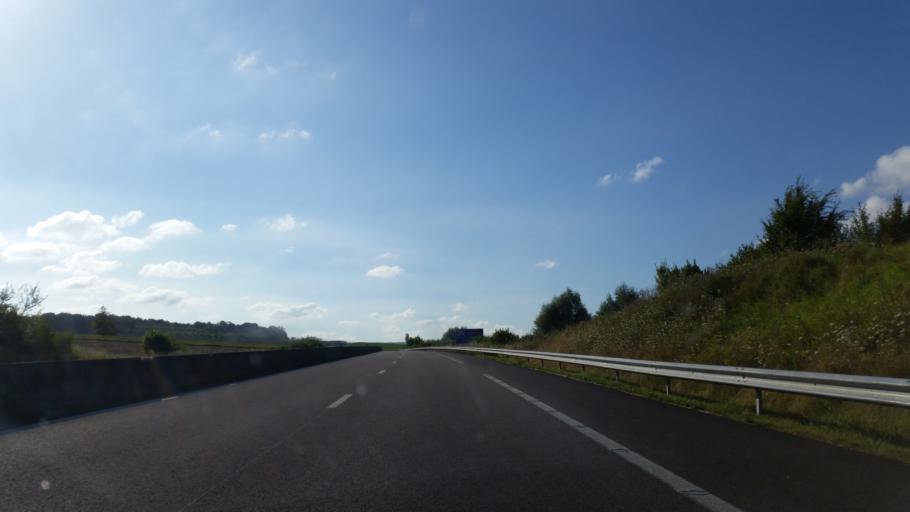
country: FR
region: Haute-Normandie
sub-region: Departement de la Seine-Maritime
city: Neufchatel-en-Bray
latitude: 49.7449
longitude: 1.5284
